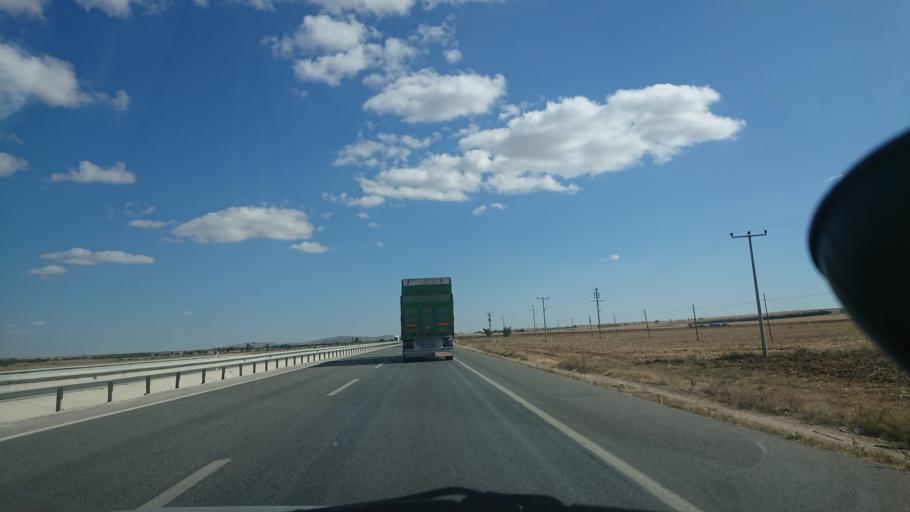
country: TR
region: Eskisehir
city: Mahmudiye
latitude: 39.5529
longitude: 30.9244
